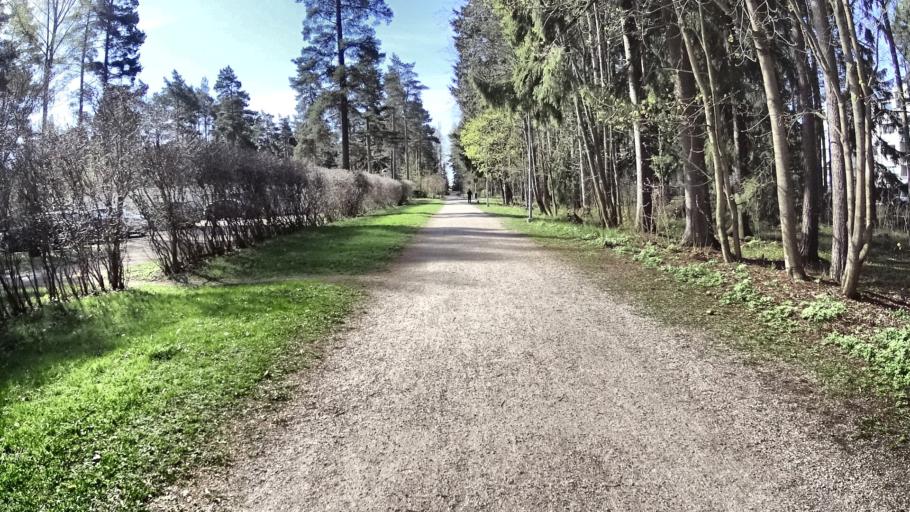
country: FI
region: Uusimaa
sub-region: Helsinki
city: Vantaa
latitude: 60.2212
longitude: 25.0626
